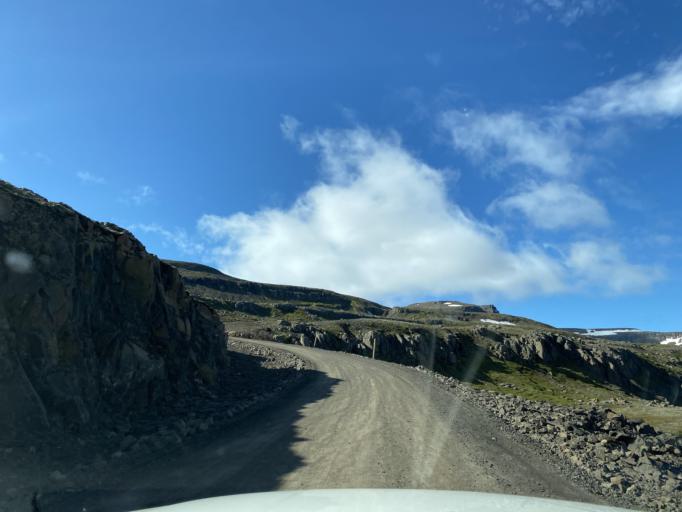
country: IS
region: East
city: Eskifjoerdur
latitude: 65.1775
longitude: -14.0979
